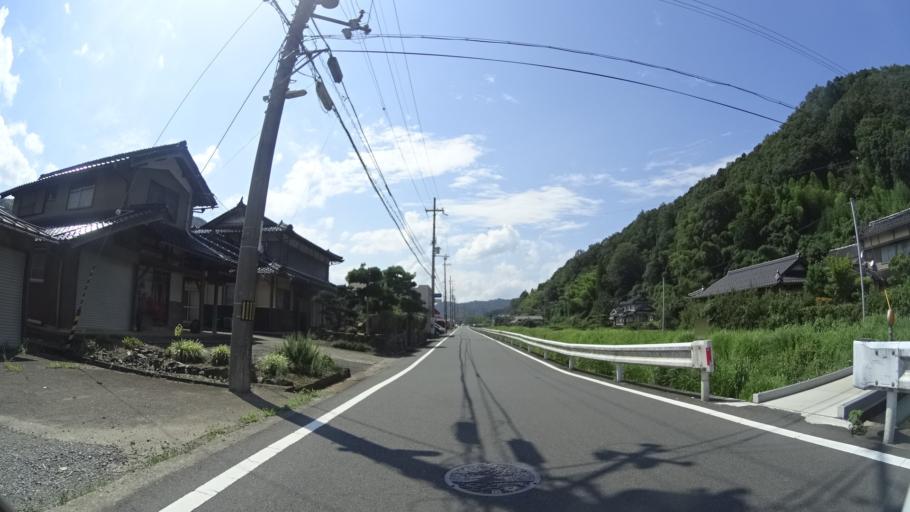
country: JP
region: Kyoto
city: Maizuru
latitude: 35.4311
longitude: 135.3169
